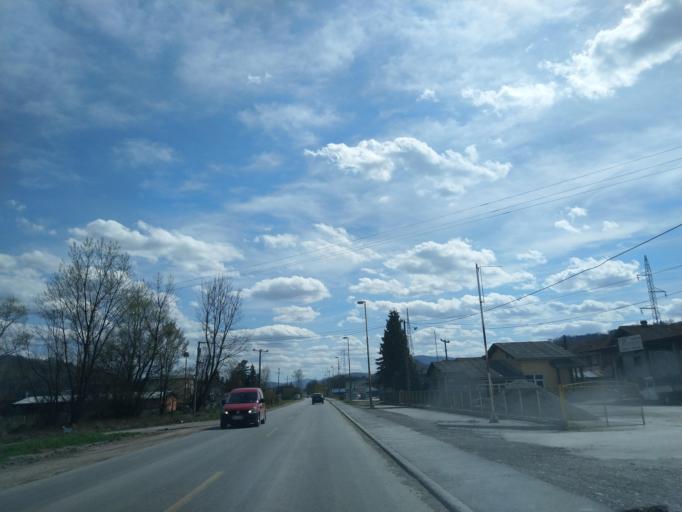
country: RS
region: Central Serbia
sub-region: Zlatiborski Okrug
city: Arilje
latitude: 43.7520
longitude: 20.1046
